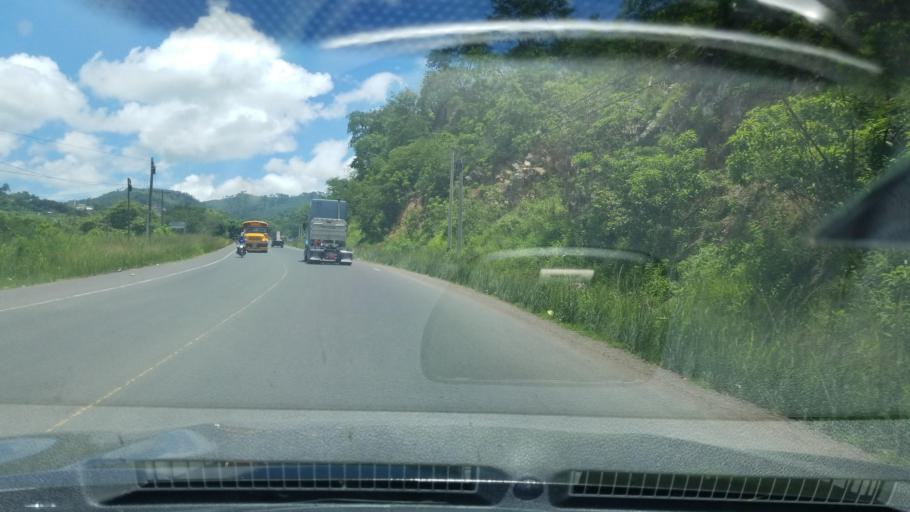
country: HN
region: Francisco Morazan
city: Rio Abajo
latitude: 14.1448
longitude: -87.2176
